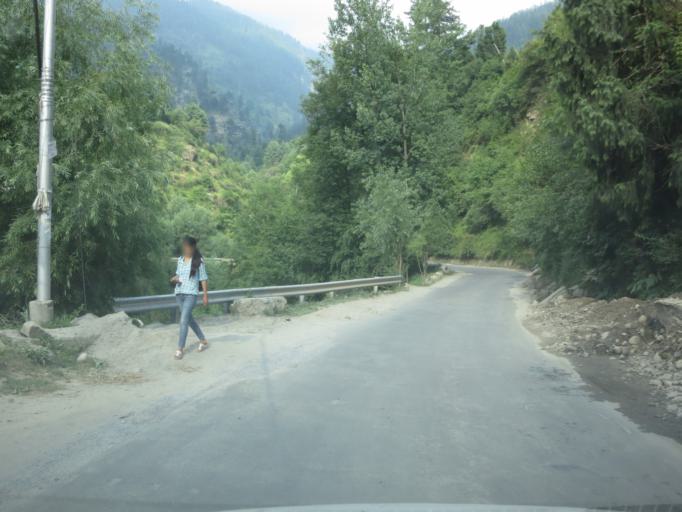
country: IN
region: Himachal Pradesh
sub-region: Kulu
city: Manali
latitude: 32.2195
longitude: 77.1988
